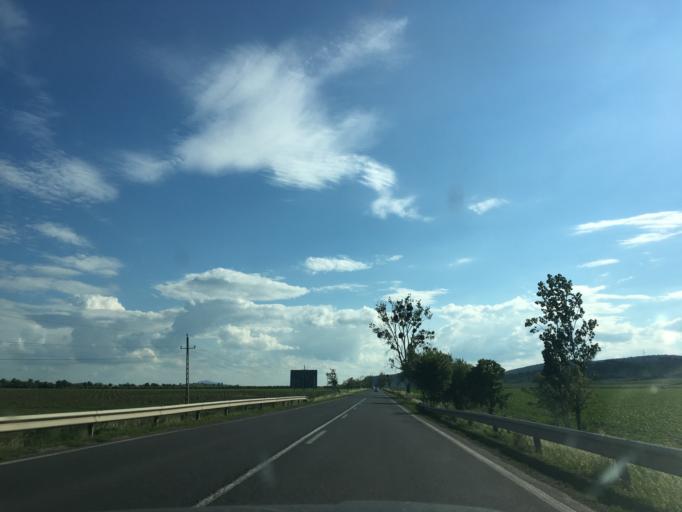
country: HU
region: Borsod-Abauj-Zemplen
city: Sarospatak
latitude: 48.3149
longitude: 21.5349
